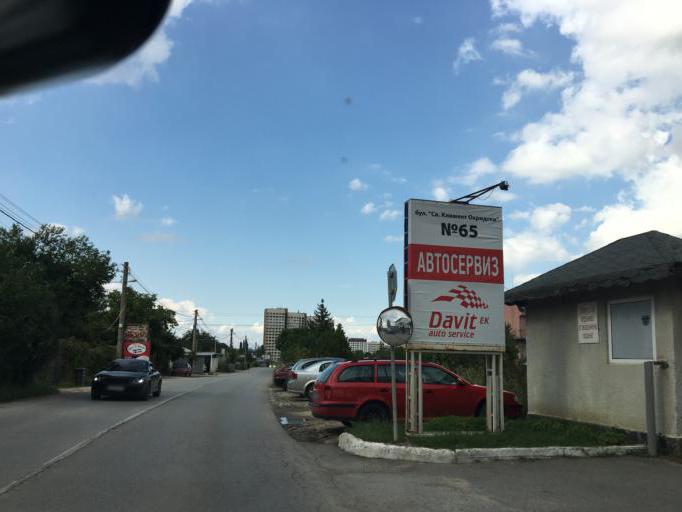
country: BG
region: Sofia-Capital
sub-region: Stolichna Obshtina
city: Sofia
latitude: 42.6421
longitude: 23.3530
